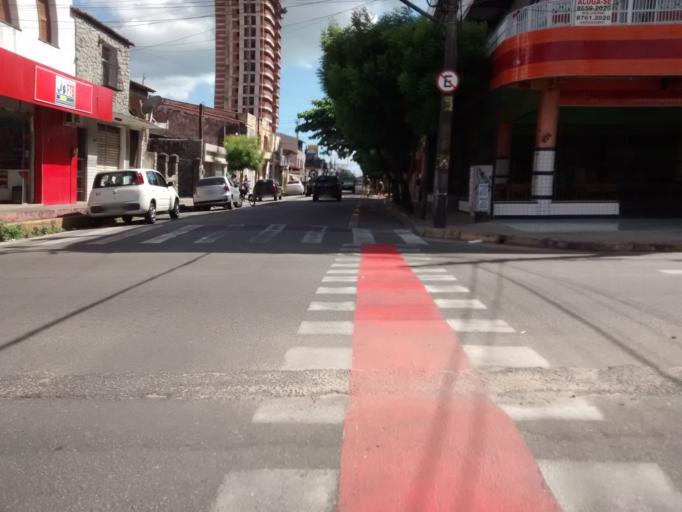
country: BR
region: Ceara
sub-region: Fortaleza
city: Fortaleza
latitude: -3.7386
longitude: -38.5499
